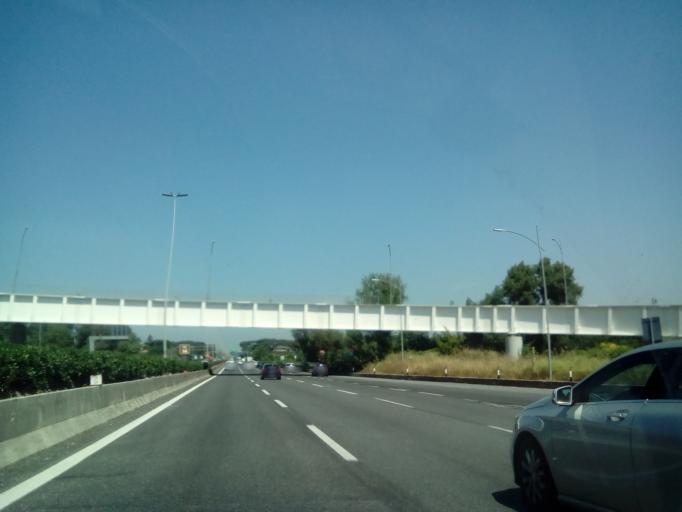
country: IT
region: Latium
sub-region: Citta metropolitana di Roma Capitale
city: Setteville
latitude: 41.9230
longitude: 12.6095
